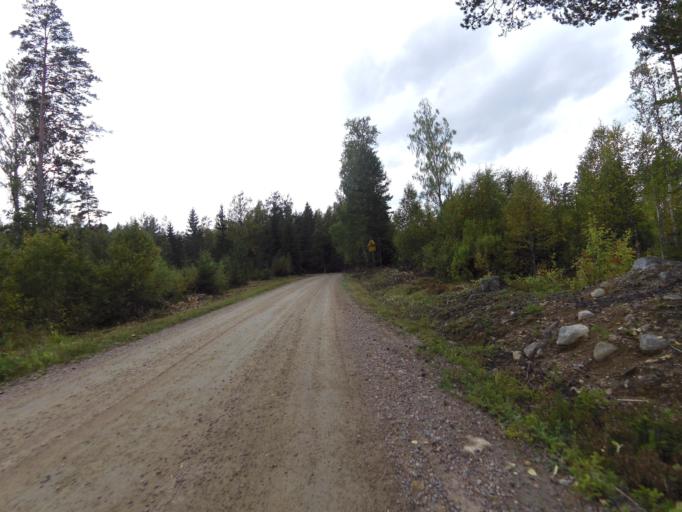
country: SE
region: Gaevleborg
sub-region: Sandvikens Kommun
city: Sandviken
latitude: 60.7563
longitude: 16.8441
